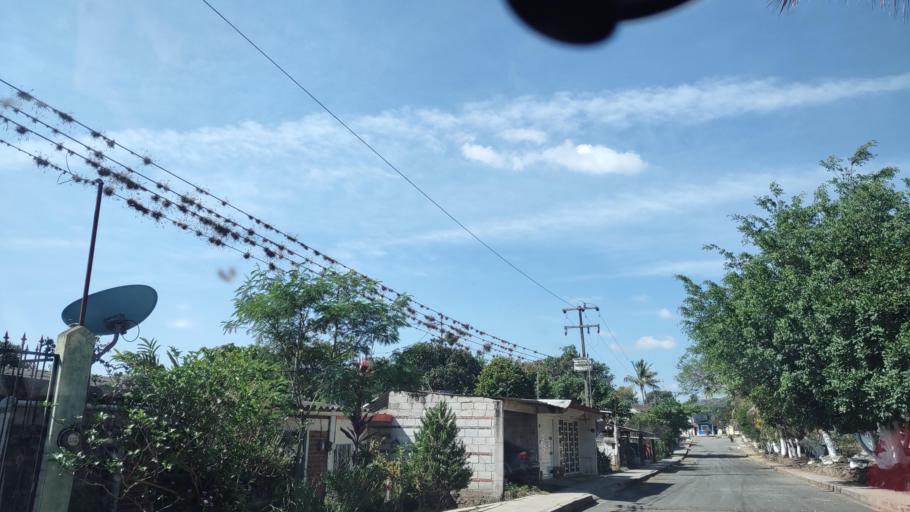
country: MX
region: Veracruz
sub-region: Coatepec
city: Tuzamapan
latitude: 19.3823
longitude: -96.9032
